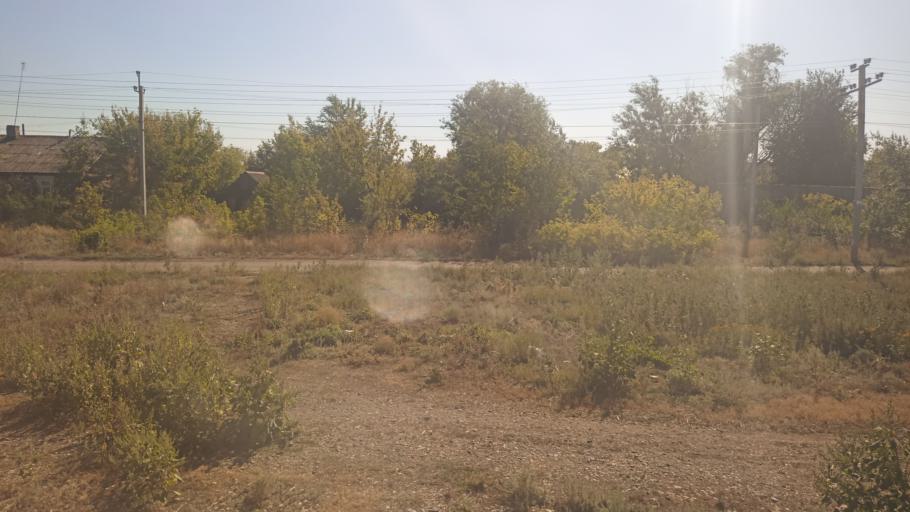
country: RU
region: Saratov
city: Pushkino
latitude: 51.2359
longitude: 46.9790
